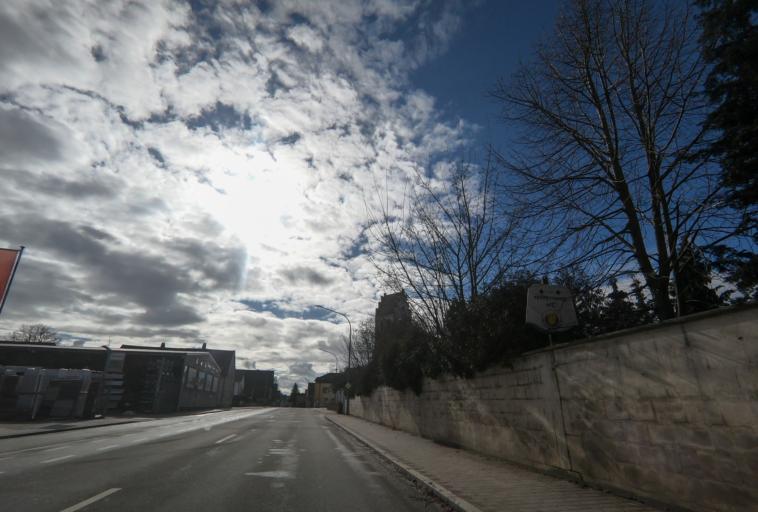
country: DE
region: Bavaria
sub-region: Lower Bavaria
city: Mallersdorf-Pfaffenberg
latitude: 48.7404
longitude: 12.1930
